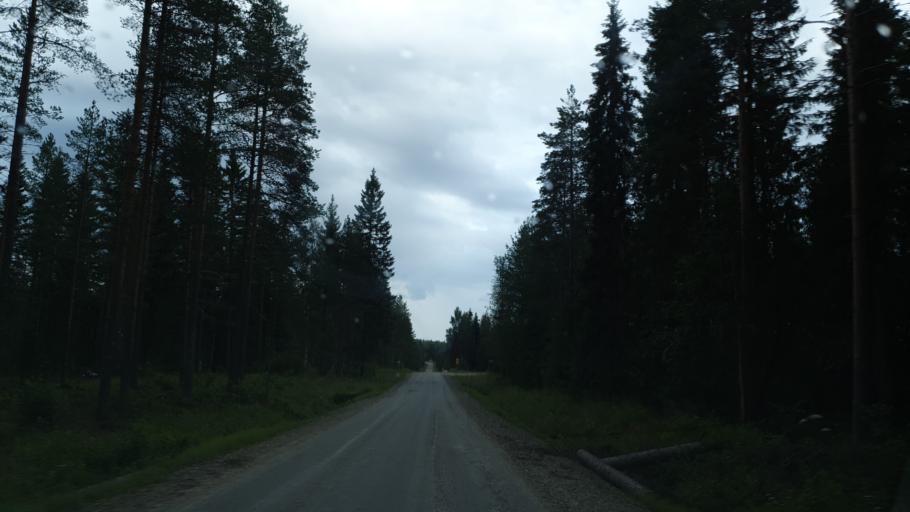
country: FI
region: Kainuu
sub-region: Kehys-Kainuu
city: Kuhmo
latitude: 64.2127
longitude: 29.3691
